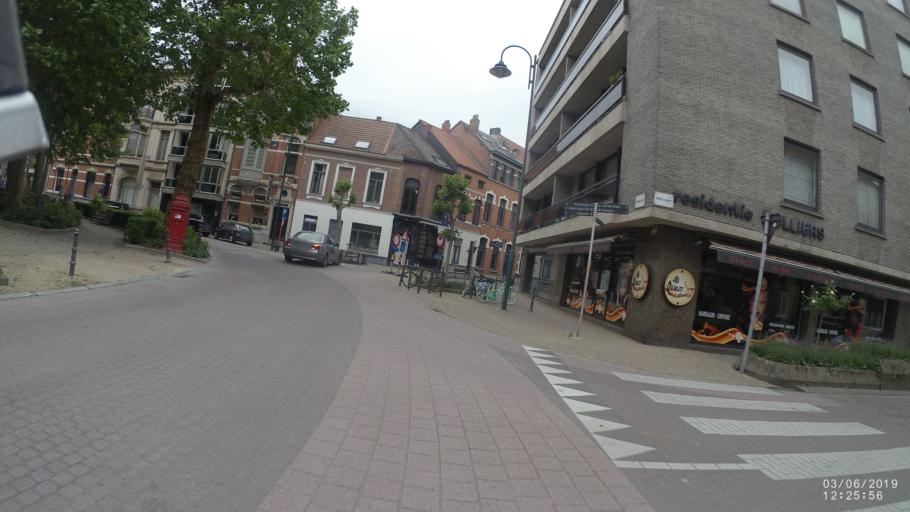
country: BE
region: Flanders
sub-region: Provincie Oost-Vlaanderen
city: Sint-Niklaas
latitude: 51.1686
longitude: 4.1449
